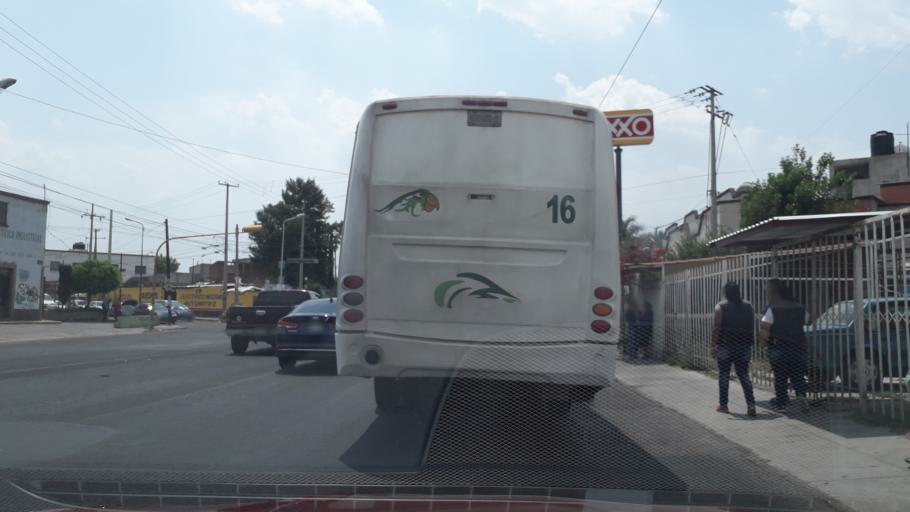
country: MX
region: Puebla
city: Puebla
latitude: 19.0446
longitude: -98.1844
